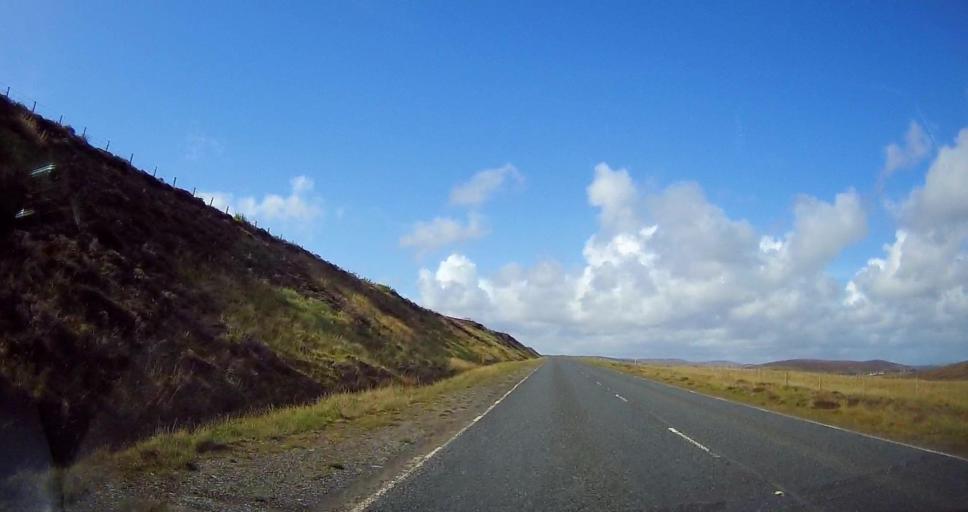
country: GB
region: Scotland
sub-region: Shetland Islands
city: Lerwick
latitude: 60.2155
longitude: -1.2339
